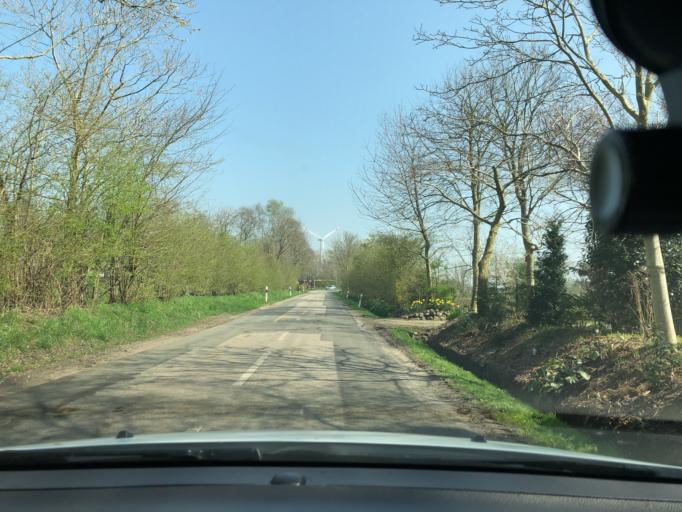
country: DE
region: Schleswig-Holstein
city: Grossenwiehe
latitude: 54.6732
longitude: 9.2662
